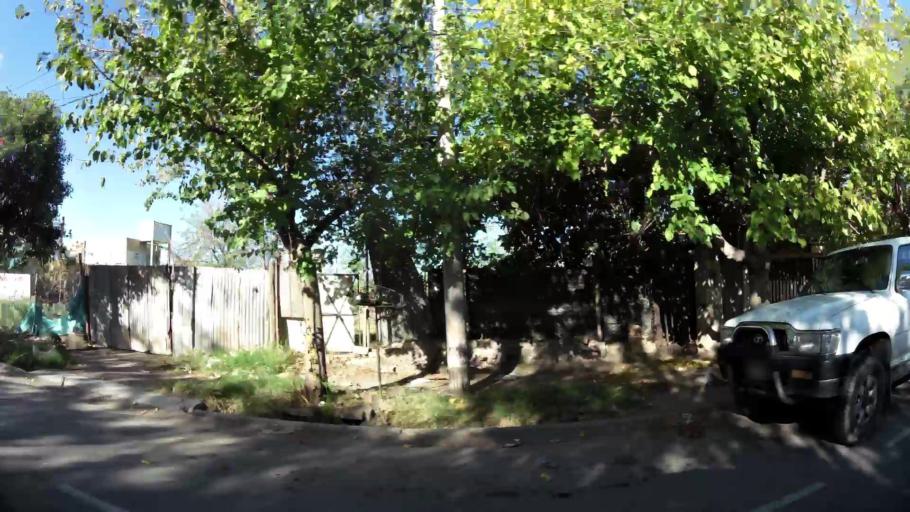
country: AR
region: San Juan
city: Villa Krause
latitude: -31.5682
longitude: -68.5201
